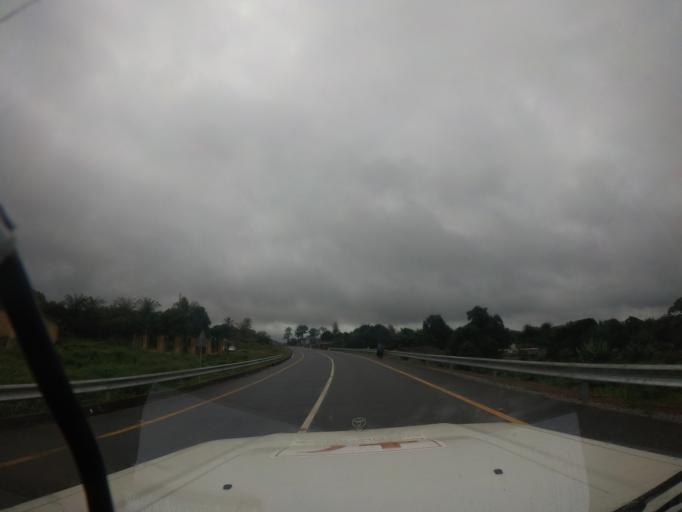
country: SL
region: Eastern Province
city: Hangha
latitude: 7.9375
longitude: -11.1434
